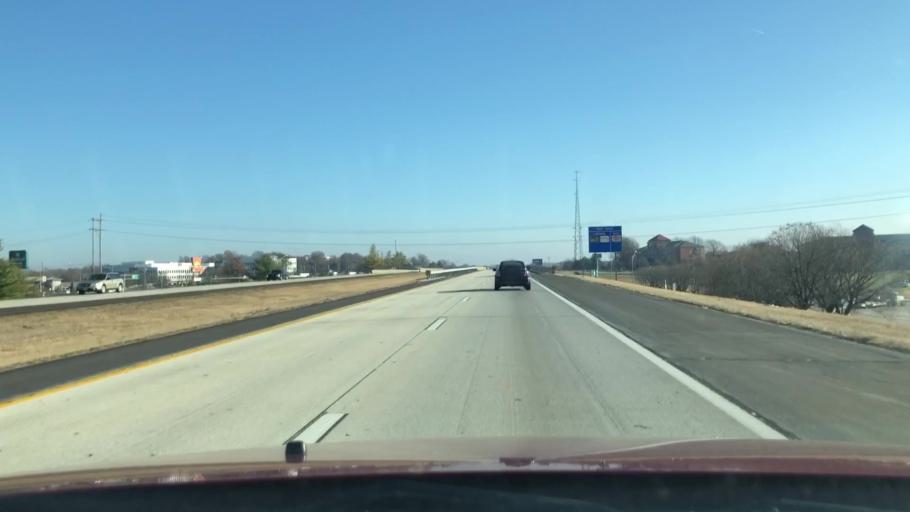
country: US
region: Missouri
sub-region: Greene County
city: Battlefield
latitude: 37.1355
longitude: -93.2987
